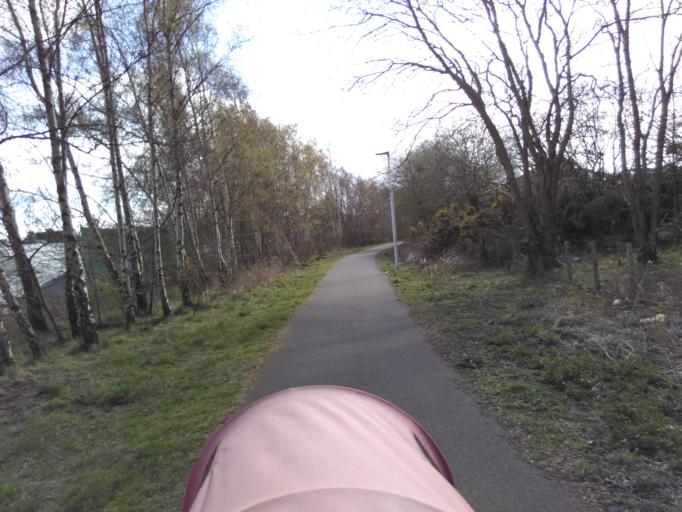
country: GB
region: Scotland
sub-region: Midlothian
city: Loanhead
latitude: 55.8804
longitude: -3.1442
